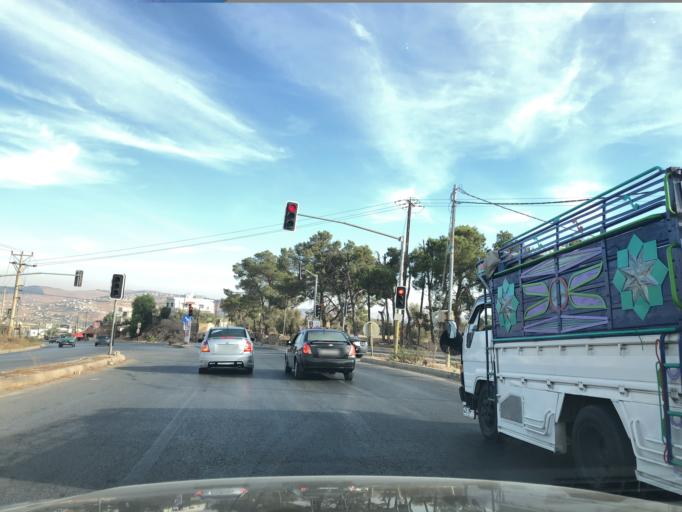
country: JO
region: Irbid
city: Al Kittah
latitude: 32.2779
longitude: 35.8691
